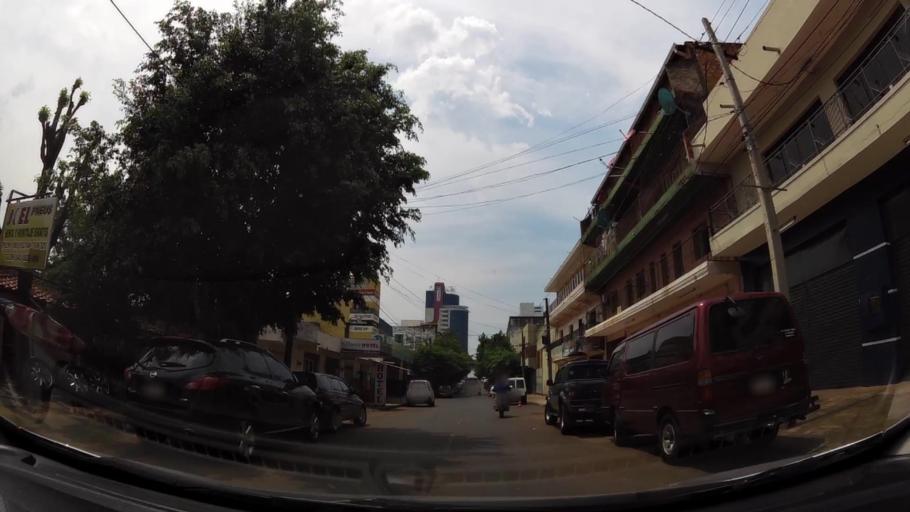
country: PY
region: Alto Parana
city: Ciudad del Este
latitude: -25.5076
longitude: -54.6142
